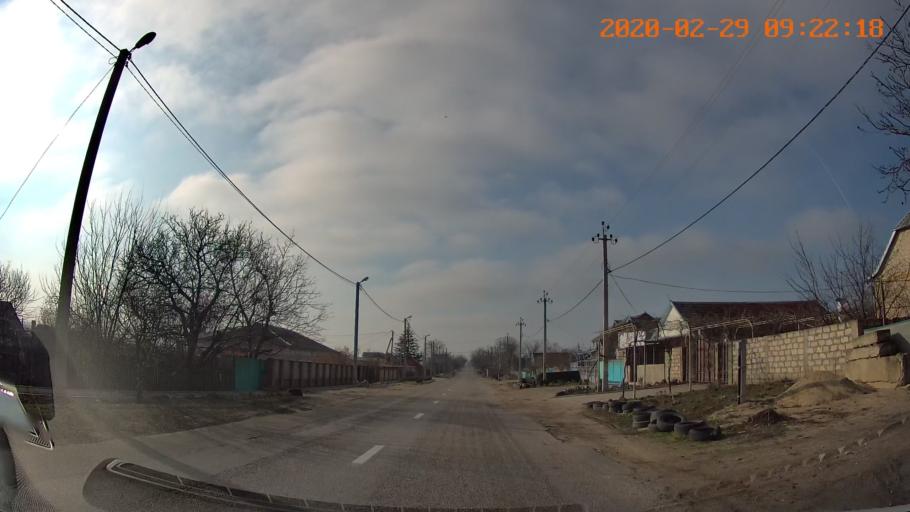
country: MD
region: Telenesti
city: Pervomaisc
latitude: 46.7364
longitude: 29.9644
